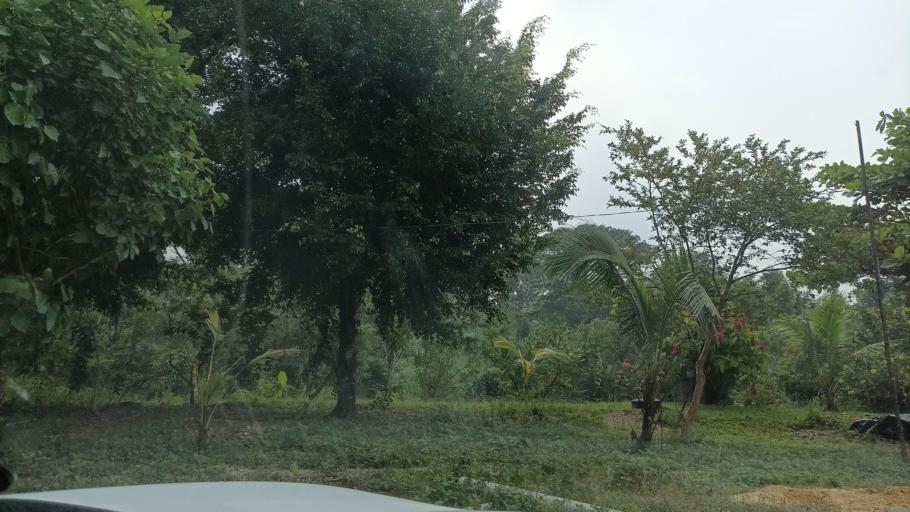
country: MX
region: Veracruz
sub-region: Moloacan
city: Cuichapa
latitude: 17.5852
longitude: -94.2353
